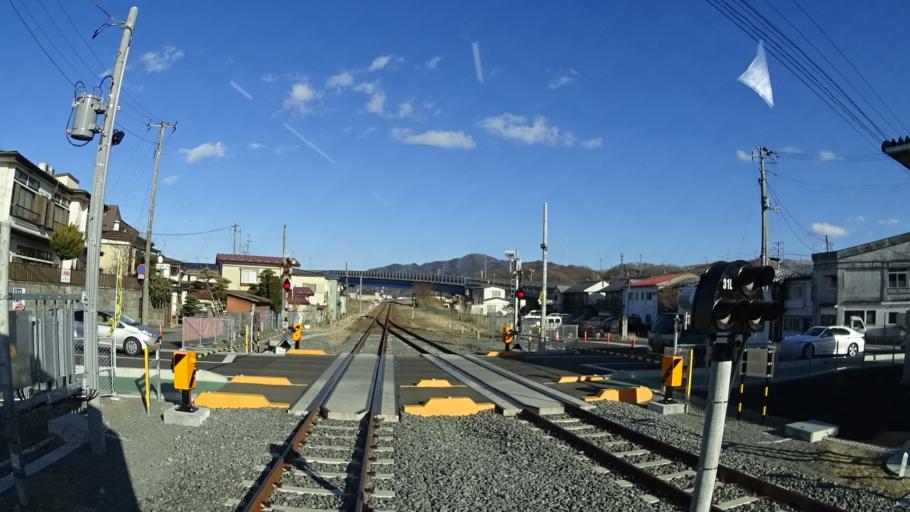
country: JP
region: Iwate
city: Miyako
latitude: 39.6395
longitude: 141.9499
